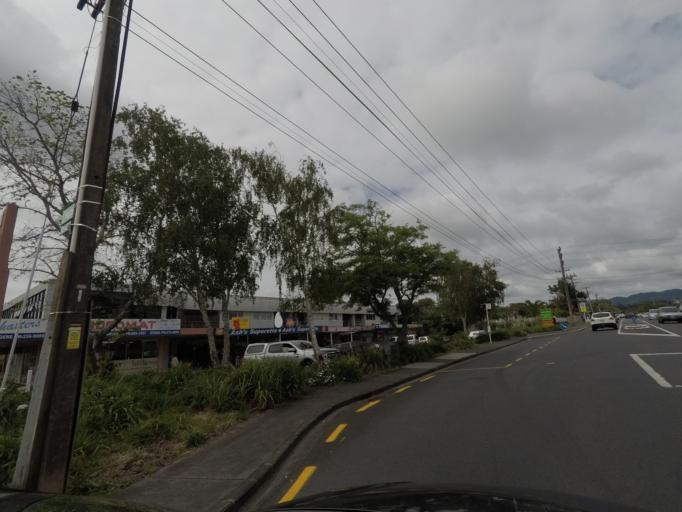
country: NZ
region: Auckland
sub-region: Auckland
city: Waitakere
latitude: -36.8963
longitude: 174.6268
